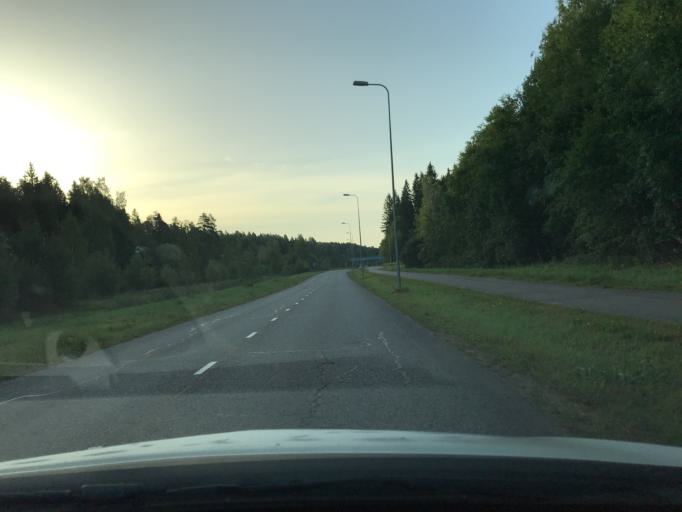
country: FI
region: Uusimaa
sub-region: Helsinki
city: Vihti
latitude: 60.4036
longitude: 24.4864
